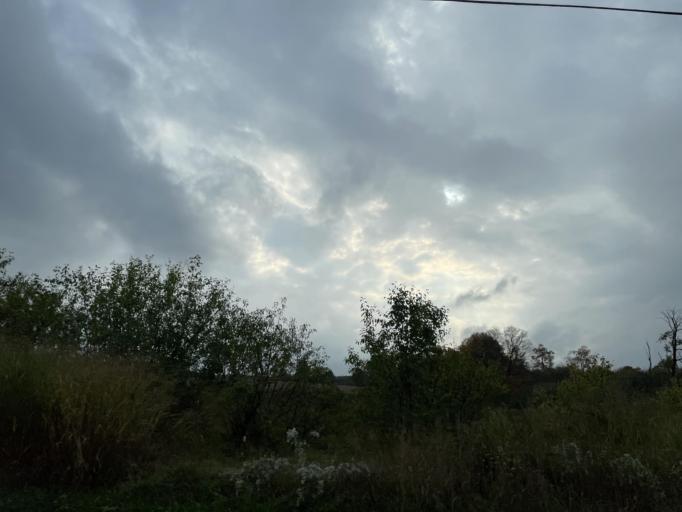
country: CA
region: Ontario
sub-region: Wellington County
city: Guelph
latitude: 43.5258
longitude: -80.1880
